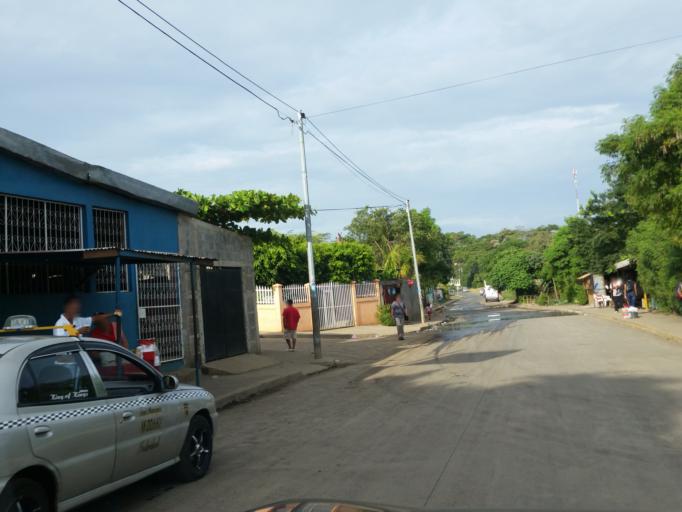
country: NI
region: Managua
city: Managua
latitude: 12.0993
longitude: -86.2265
